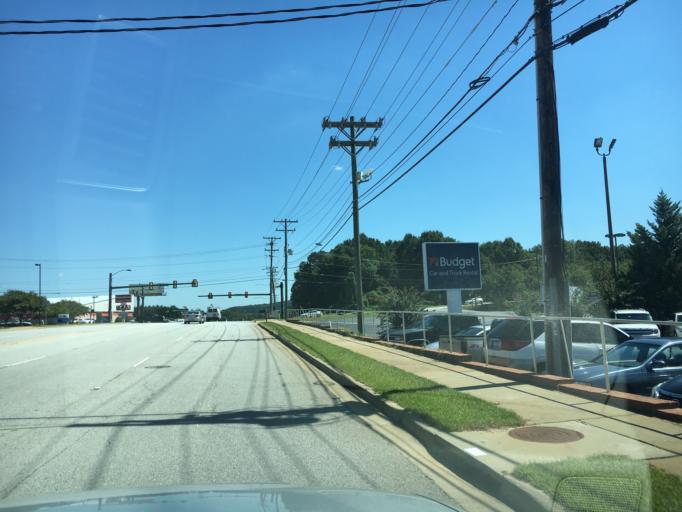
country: US
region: South Carolina
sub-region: Greenville County
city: Greenville
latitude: 34.8355
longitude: -82.3358
